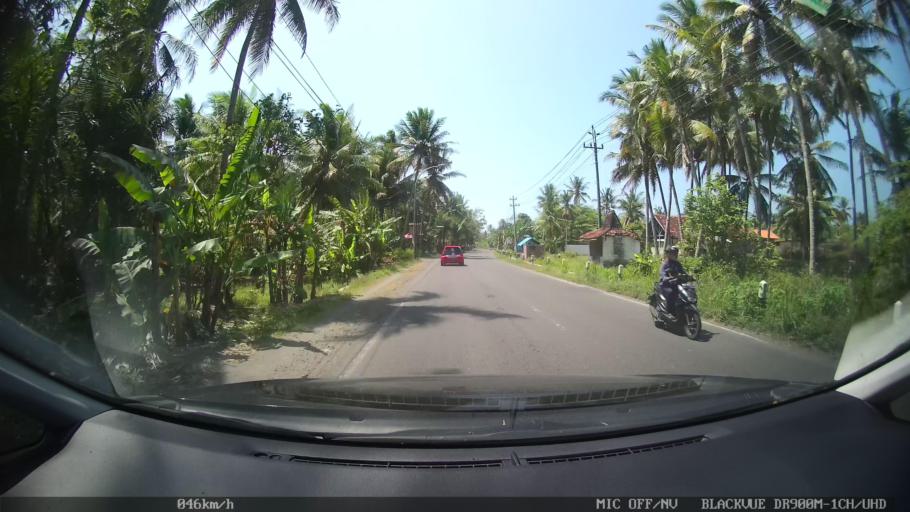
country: ID
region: Daerah Istimewa Yogyakarta
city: Srandakan
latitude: -7.9274
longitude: 110.1286
